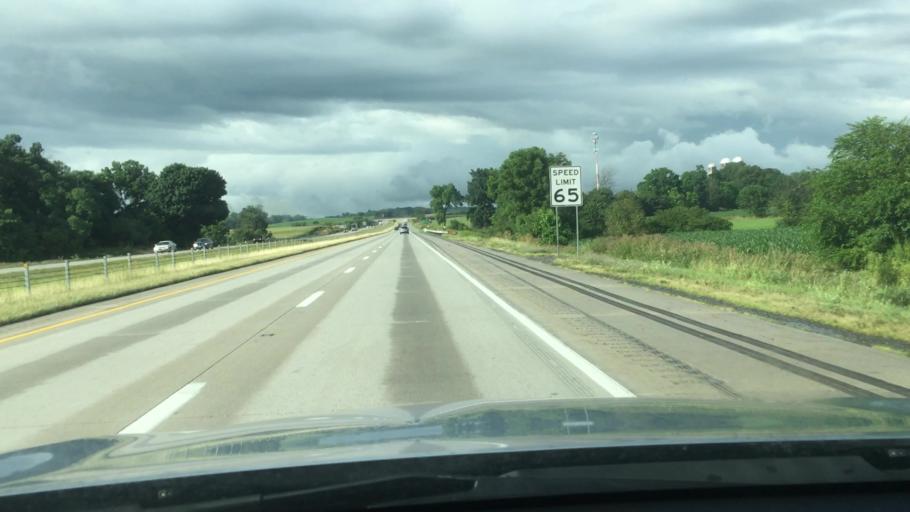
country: US
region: Pennsylvania
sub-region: Franklin County
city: Scotland
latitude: 39.9709
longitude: -77.5740
